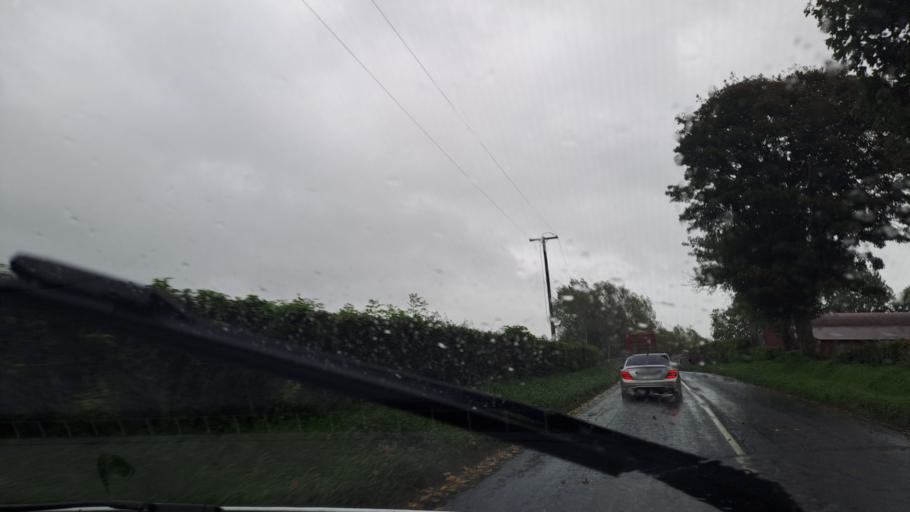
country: IE
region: Ulster
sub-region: County Monaghan
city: Carrickmacross
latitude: 53.9769
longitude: -6.6499
